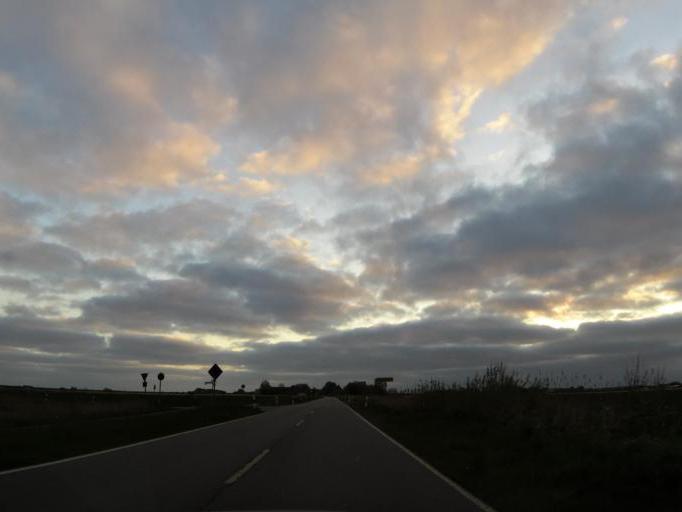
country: DE
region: Schleswig-Holstein
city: Ockholm
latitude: 54.6653
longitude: 8.8370
